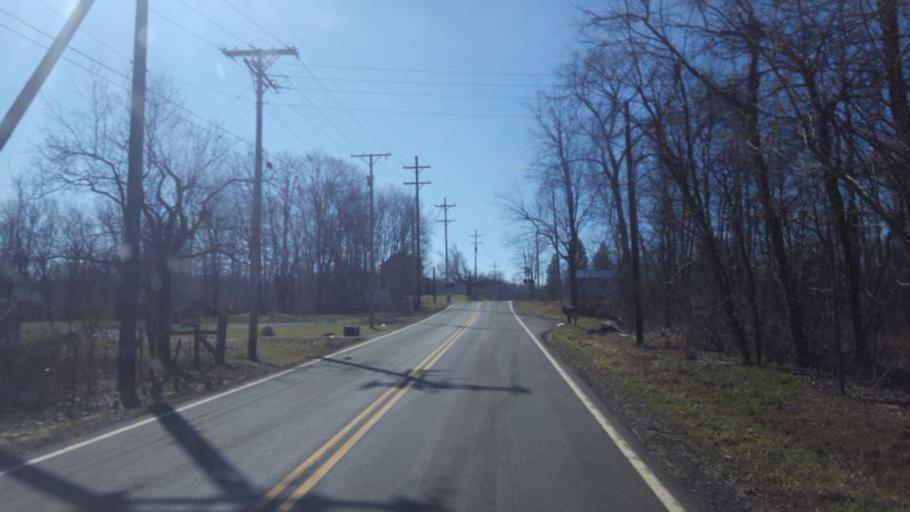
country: US
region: Ohio
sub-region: Richland County
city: Lincoln Heights
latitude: 40.8269
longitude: -82.4788
